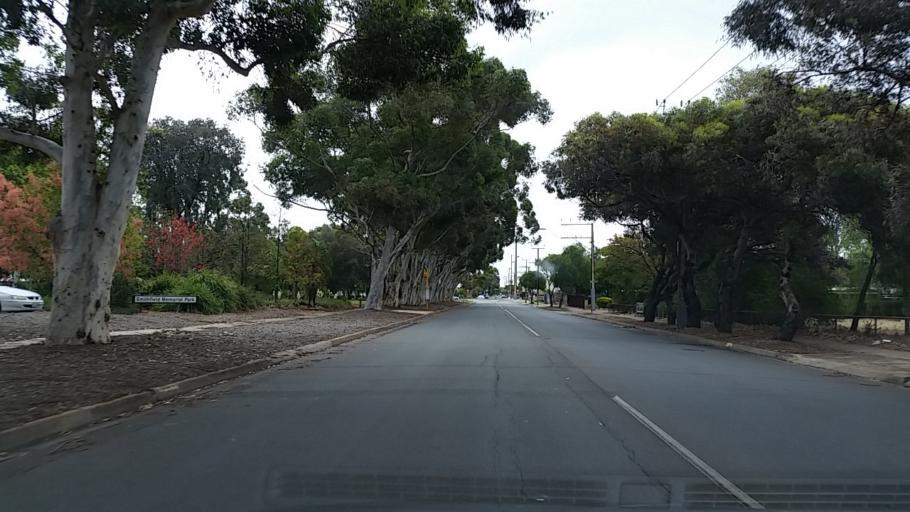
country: AU
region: South Australia
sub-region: Playford
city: Smithfield
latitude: -34.6830
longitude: 138.6912
